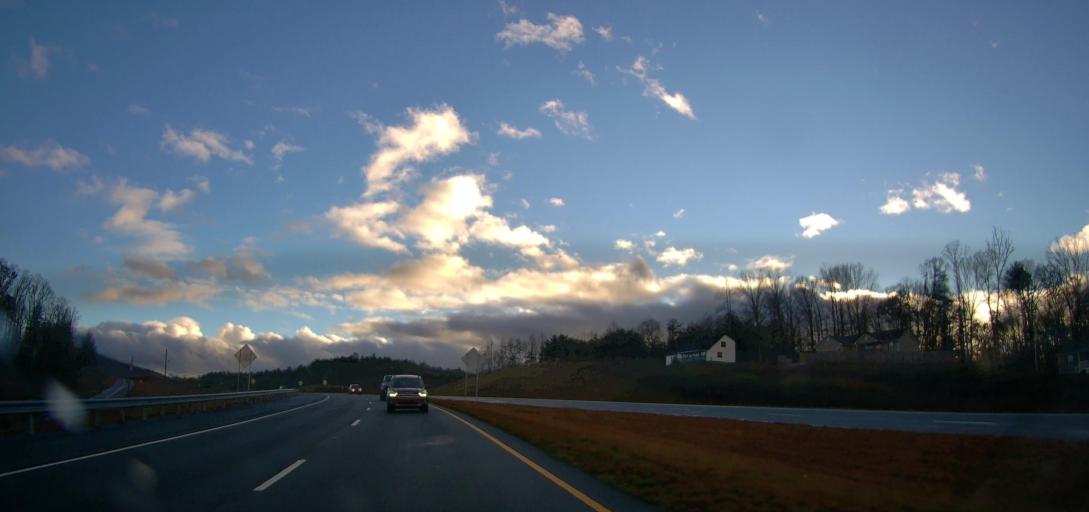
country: US
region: Georgia
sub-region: White County
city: Cleveland
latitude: 34.6066
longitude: -83.7818
